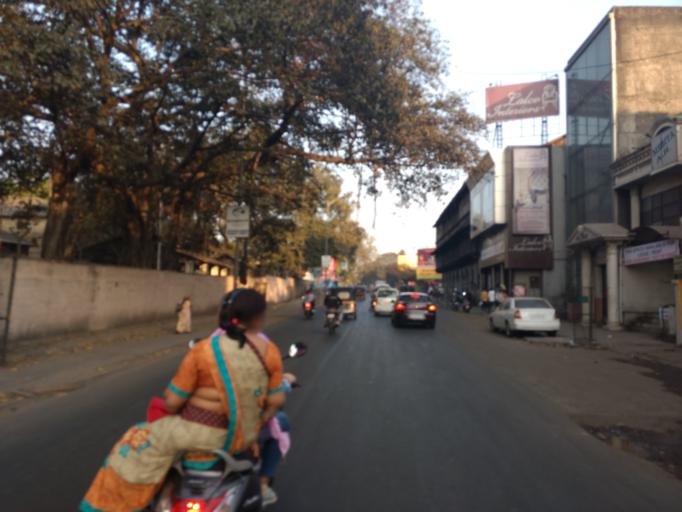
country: IN
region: Maharashtra
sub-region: Pune Division
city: Pune
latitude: 18.5067
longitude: 73.8810
